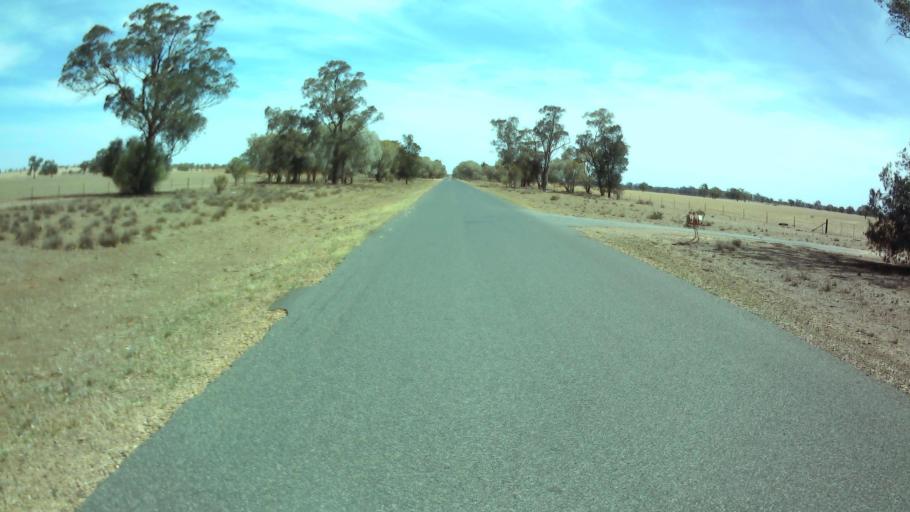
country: AU
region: New South Wales
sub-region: Weddin
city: Grenfell
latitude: -33.8682
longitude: 147.7452
